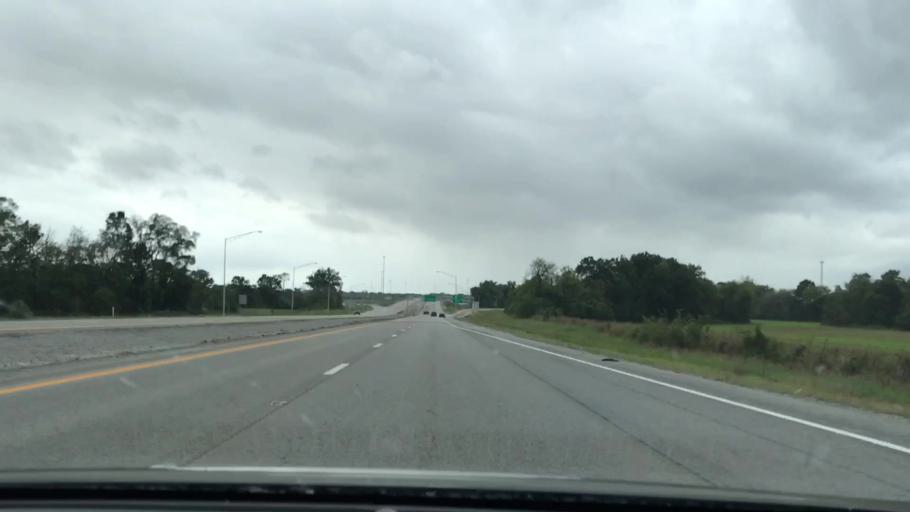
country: US
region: Kentucky
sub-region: Christian County
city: Hopkinsville
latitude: 36.8254
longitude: -87.4778
